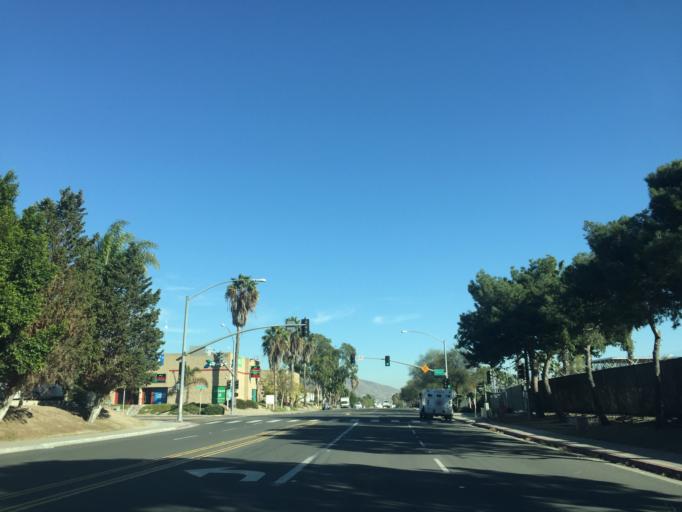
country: MX
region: Baja California
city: Tijuana
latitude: 32.5529
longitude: -116.9366
